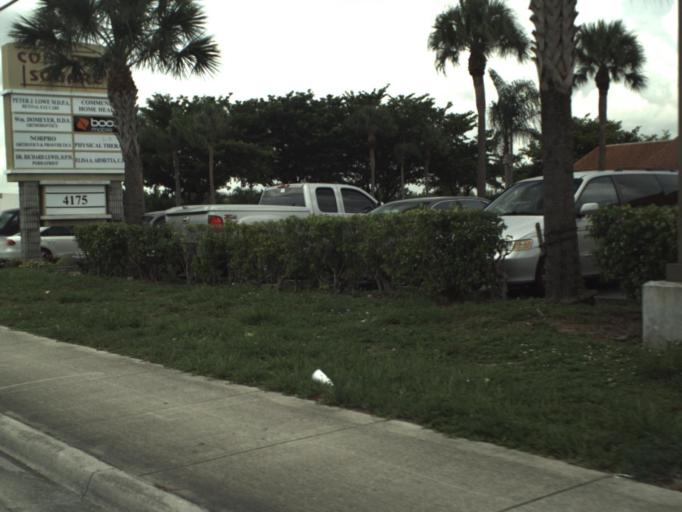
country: US
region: Florida
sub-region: Palm Beach County
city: Lake Worth Corridor
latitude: 26.6148
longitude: -80.0893
